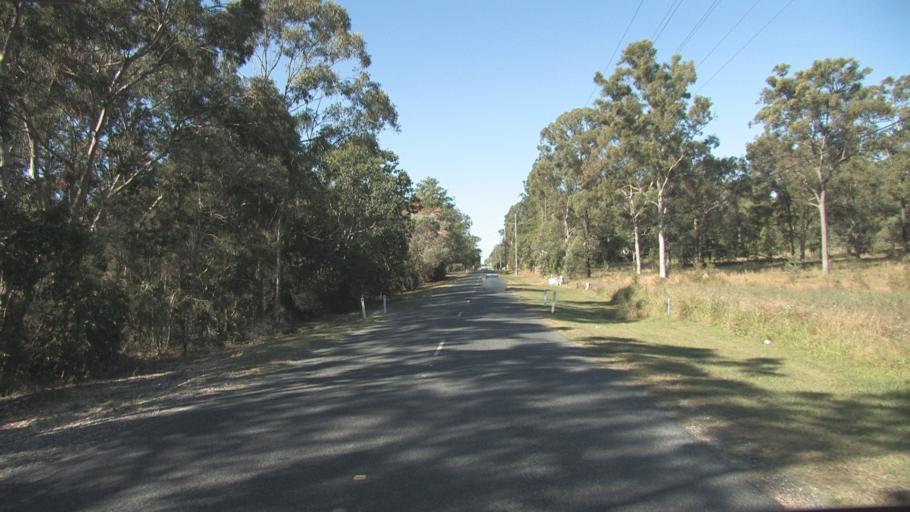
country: AU
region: Queensland
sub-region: Logan
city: Logan Reserve
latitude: -27.7119
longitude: 153.1004
